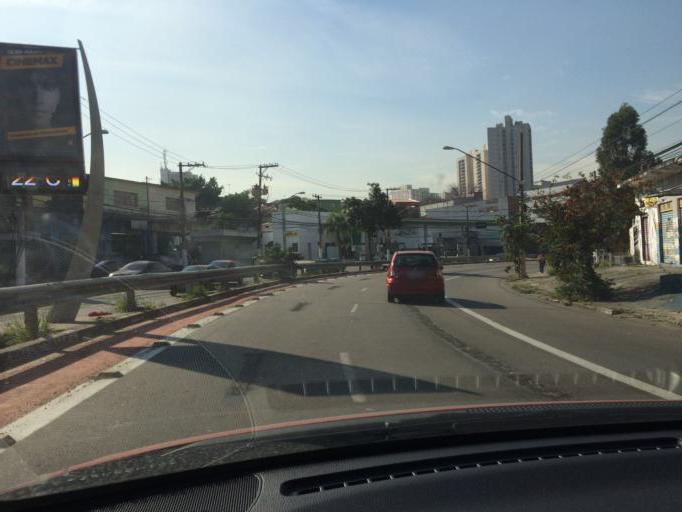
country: BR
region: Sao Paulo
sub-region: Osasco
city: Osasco
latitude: -23.5549
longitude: -46.7522
